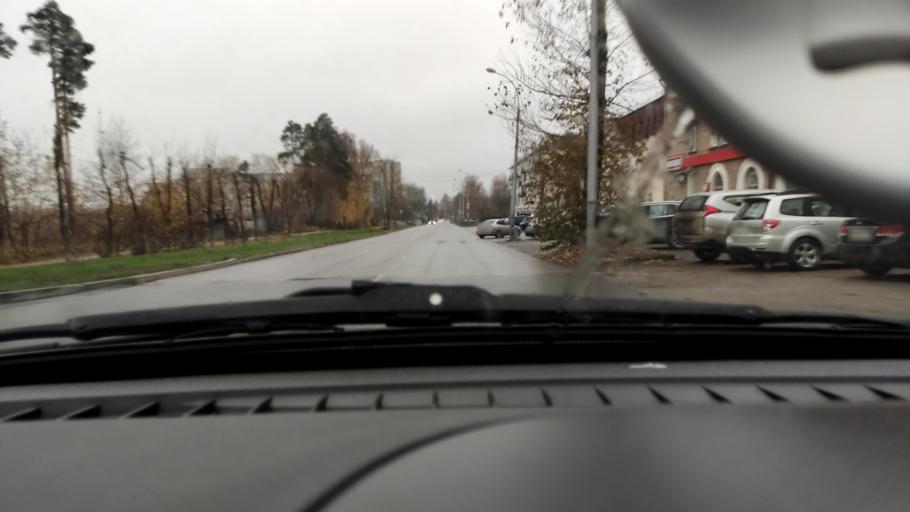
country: RU
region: Perm
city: Kultayevo
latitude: 57.9998
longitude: 55.9554
